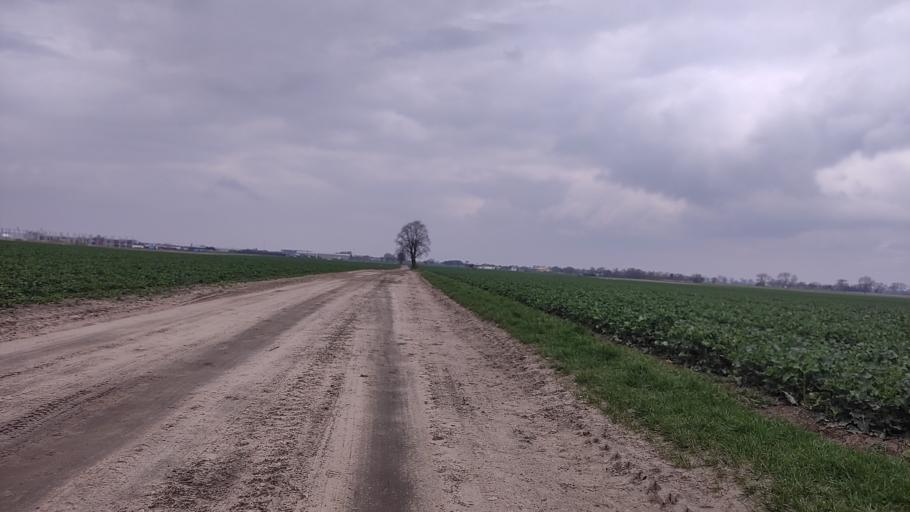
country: PL
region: Greater Poland Voivodeship
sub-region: Powiat poznanski
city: Kleszczewo
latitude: 52.4024
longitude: 17.1563
